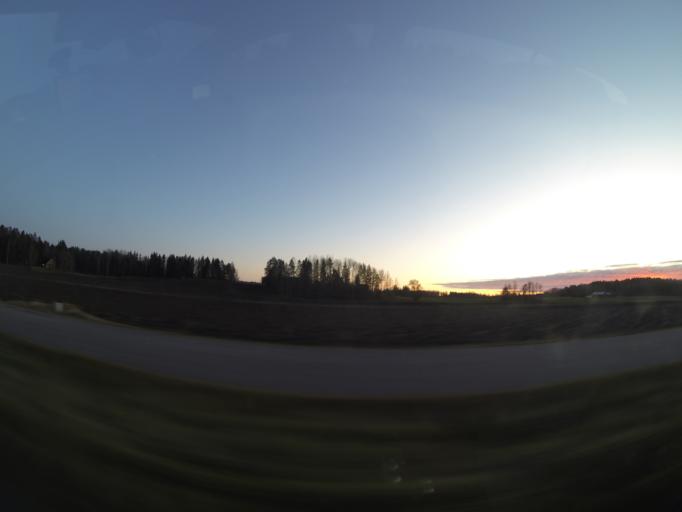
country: SE
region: OErebro
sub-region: Lindesbergs Kommun
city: Frovi
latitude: 59.3262
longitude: 15.4407
